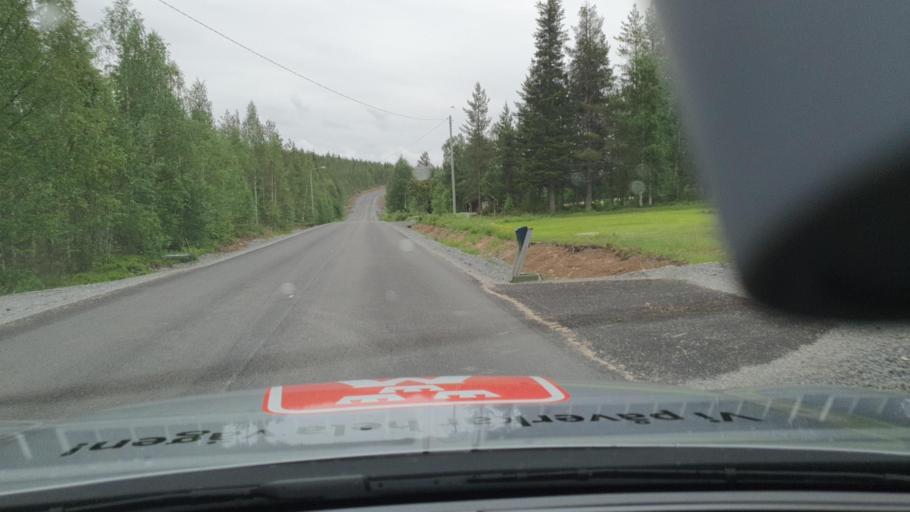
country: SE
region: Norrbotten
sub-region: Overtornea Kommun
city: OEvertornea
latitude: 66.6031
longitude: 23.3018
